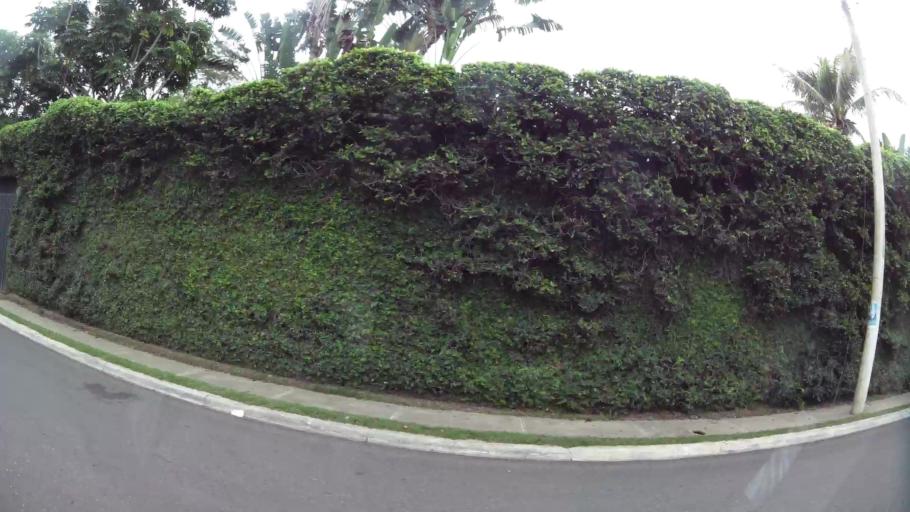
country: DO
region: Santiago
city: Santiago de los Caballeros
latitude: 19.4318
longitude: -70.6609
